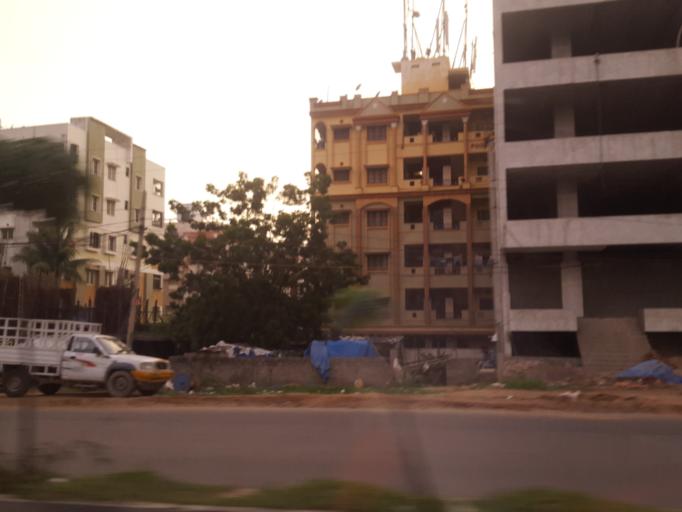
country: IN
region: Telangana
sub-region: Rangareddi
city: Kukatpalli
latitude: 17.5024
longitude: 78.3622
